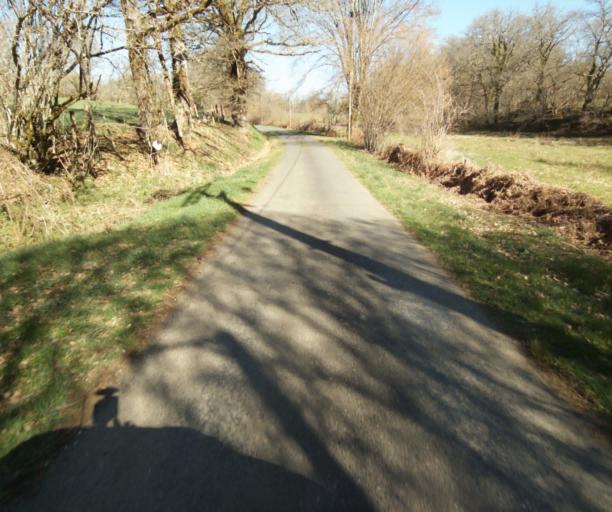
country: FR
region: Limousin
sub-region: Departement de la Correze
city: Chamboulive
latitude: 45.4128
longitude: 1.7232
